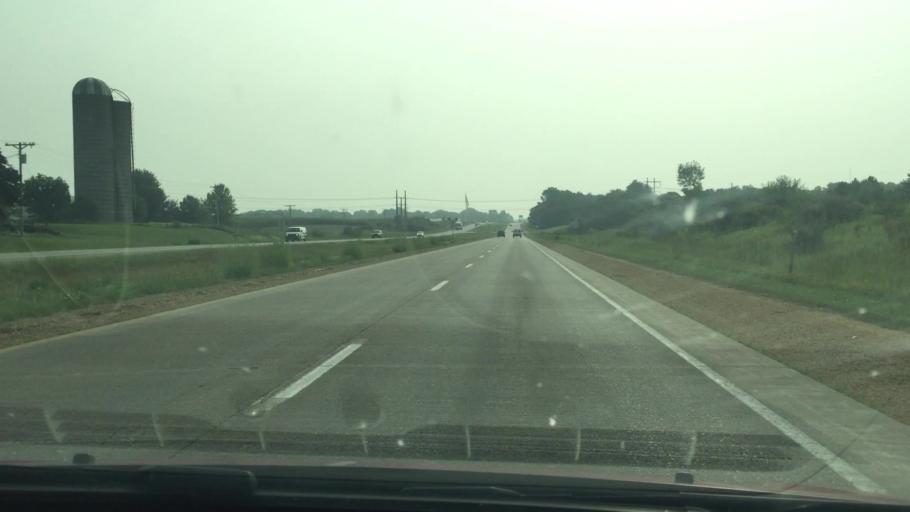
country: US
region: Iowa
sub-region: Scott County
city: Buffalo
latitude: 41.5088
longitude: -90.7053
